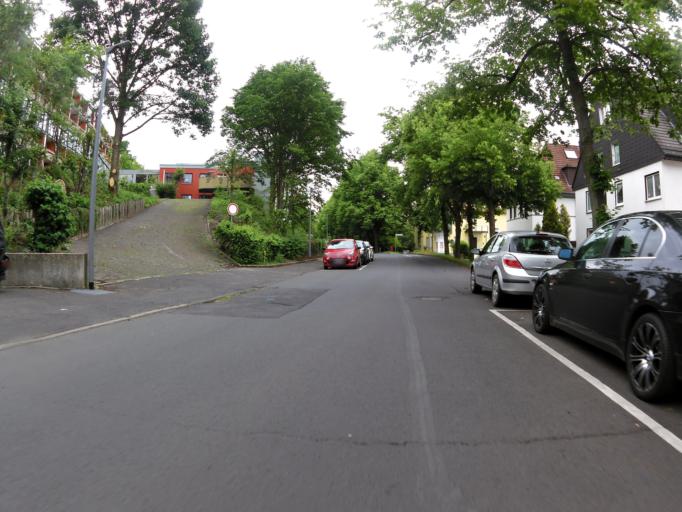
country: DE
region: Hesse
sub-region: Regierungsbezirk Kassel
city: Bad Hersfeld
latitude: 50.8579
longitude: 9.6932
